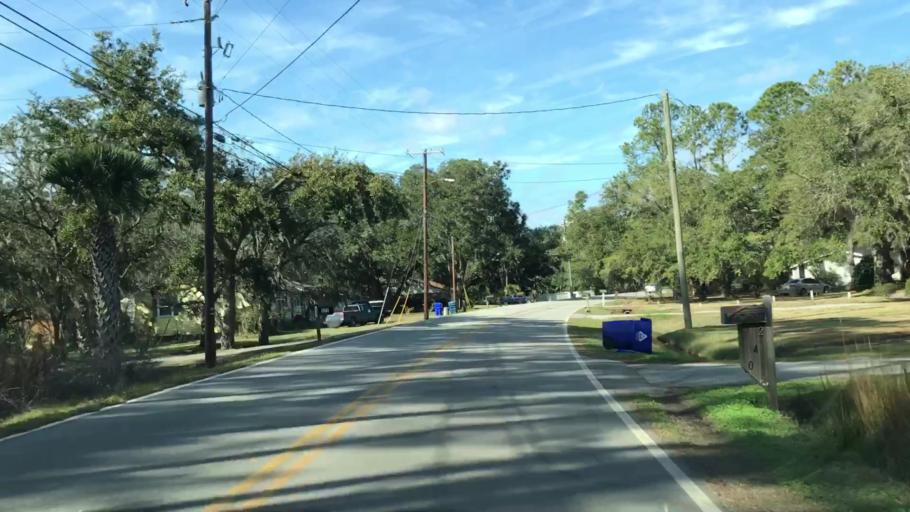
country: US
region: South Carolina
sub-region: Charleston County
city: Charleston
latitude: 32.7751
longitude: -80.0173
